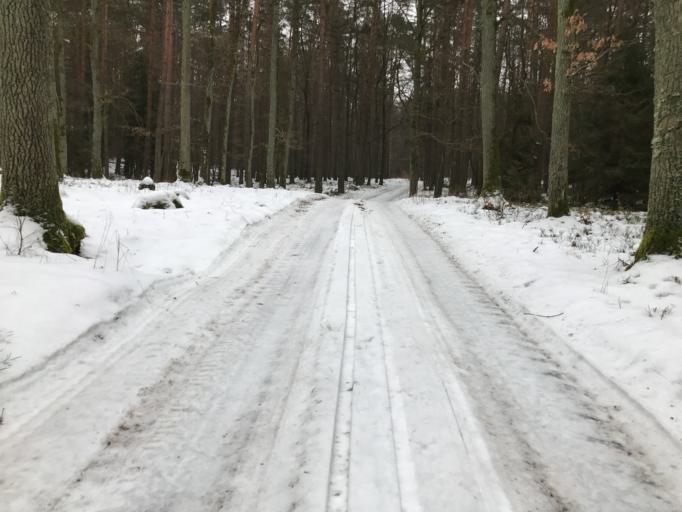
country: PL
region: Kujawsko-Pomorskie
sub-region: Powiat brodnicki
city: Gorzno
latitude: 53.1852
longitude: 19.6925
